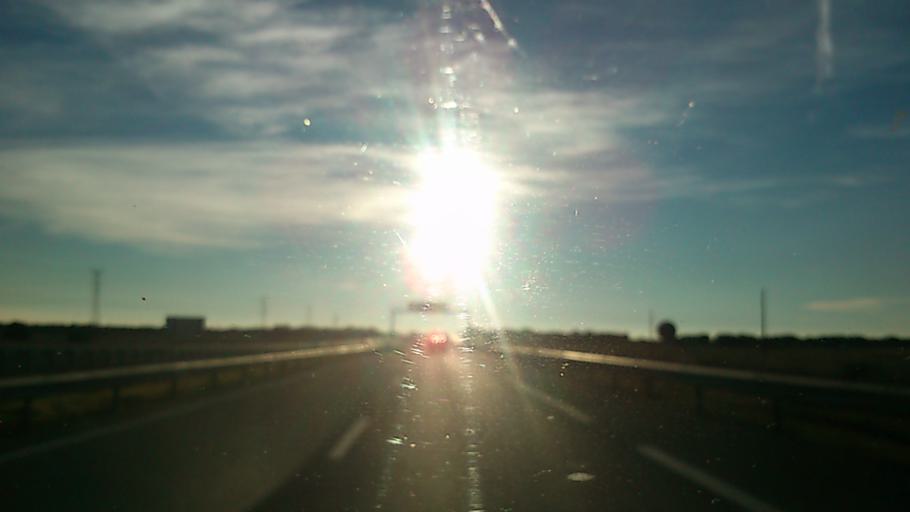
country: ES
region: Castille-La Mancha
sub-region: Provincia de Guadalajara
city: Gajanejos
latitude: 40.8339
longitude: -2.9046
